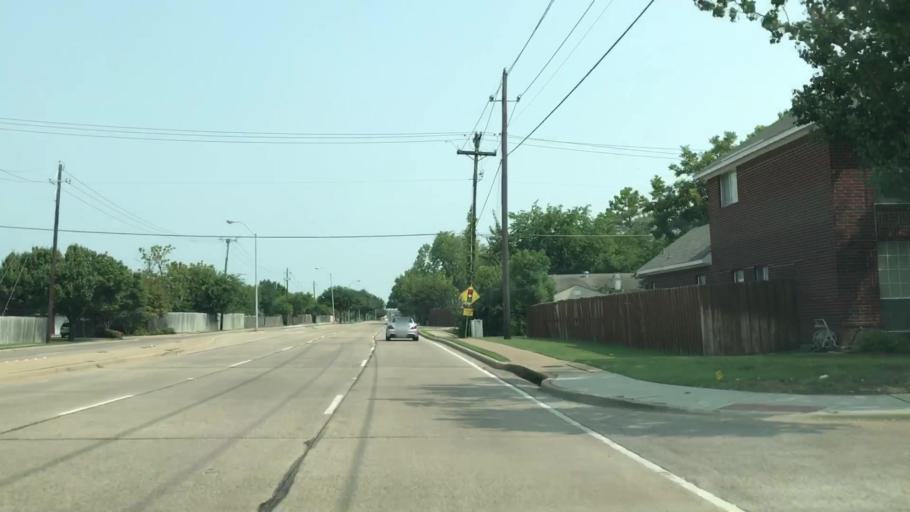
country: US
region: Texas
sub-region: Dallas County
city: Rowlett
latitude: 32.9182
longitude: -96.5743
